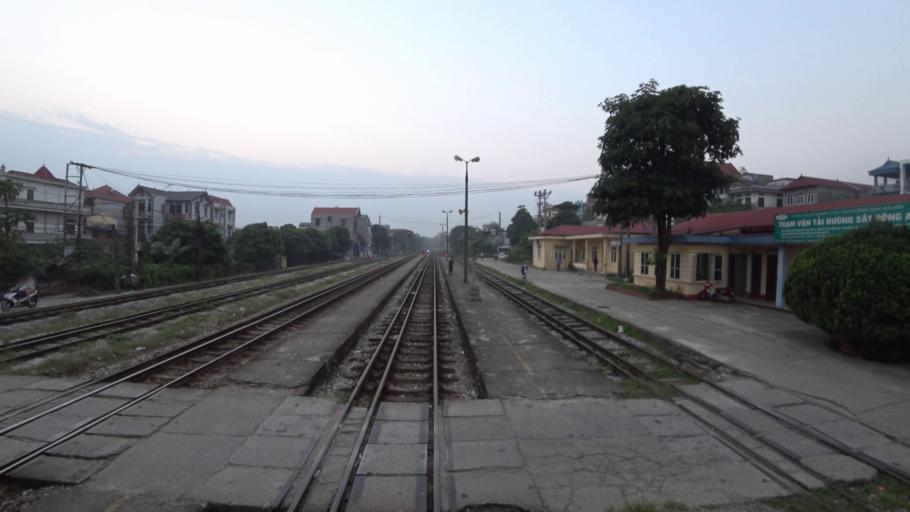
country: VN
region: Ha Noi
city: Dong Anh
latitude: 21.1932
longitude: 105.8548
